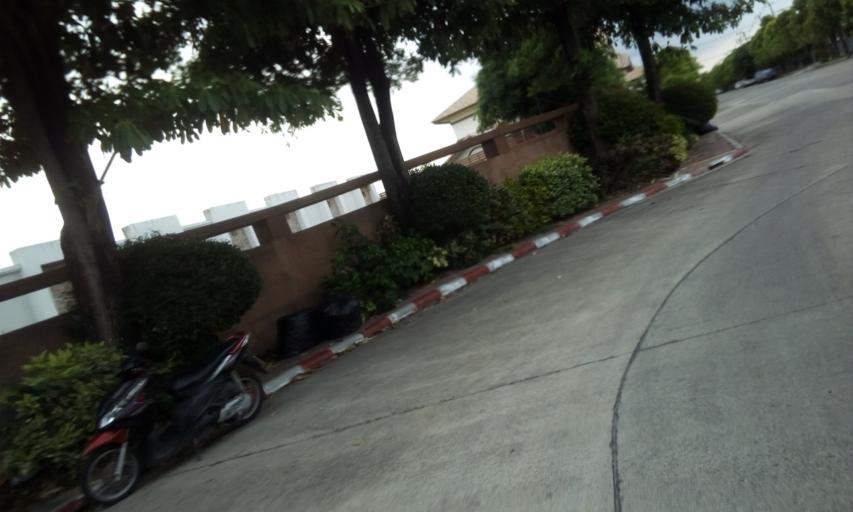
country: TH
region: Pathum Thani
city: Ban Rangsit
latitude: 14.0473
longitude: 100.8286
